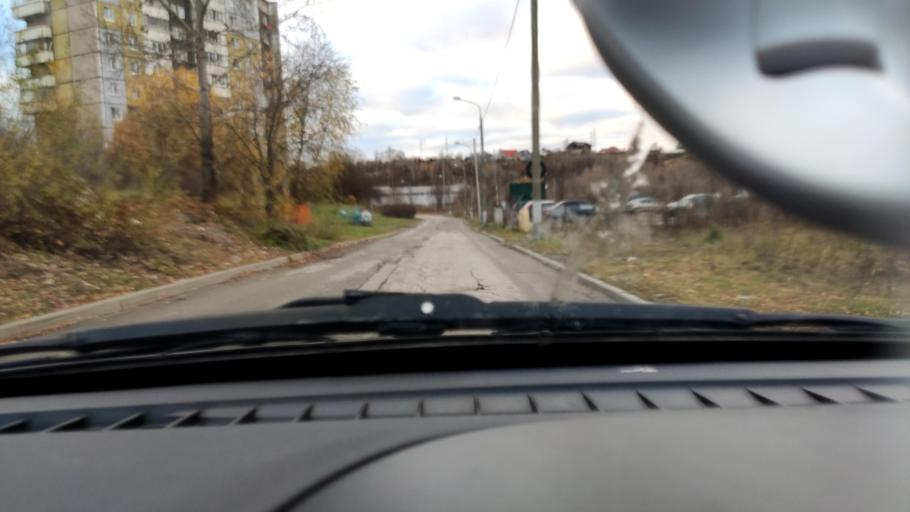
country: RU
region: Perm
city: Perm
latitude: 58.0088
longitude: 56.3137
